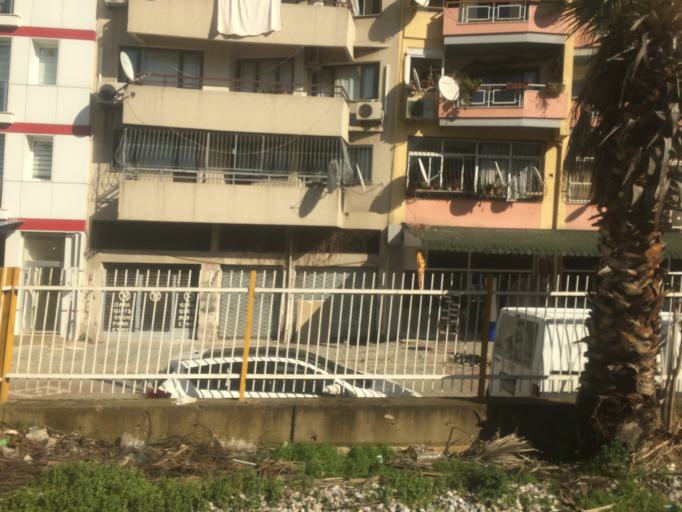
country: TR
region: Izmir
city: Karsiyaka
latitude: 38.4657
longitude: 27.1629
